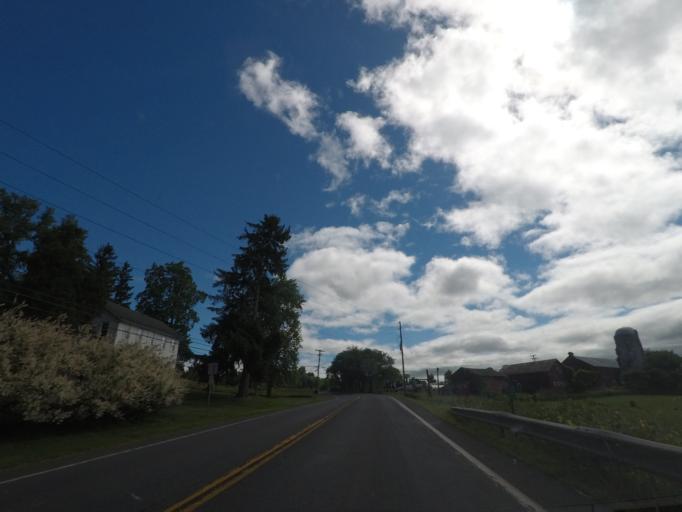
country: US
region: New York
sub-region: Columbia County
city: Philmont
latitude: 42.1384
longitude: -73.5269
